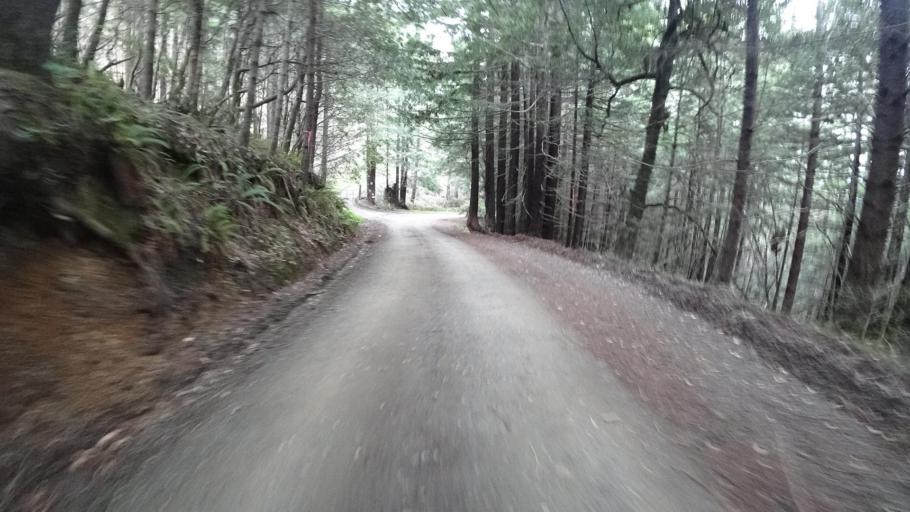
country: US
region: California
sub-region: Humboldt County
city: Redway
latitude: 40.3090
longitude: -123.8194
